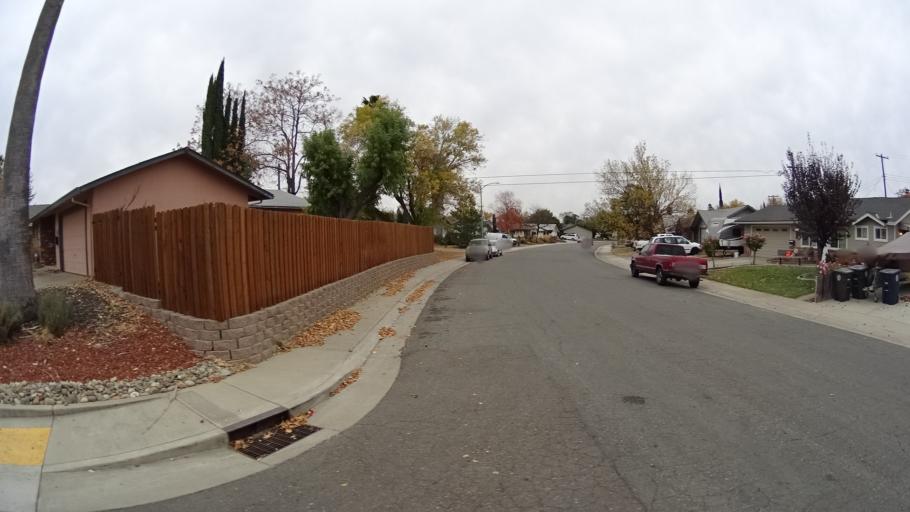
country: US
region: California
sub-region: Sacramento County
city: Citrus Heights
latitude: 38.6964
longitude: -121.2981
